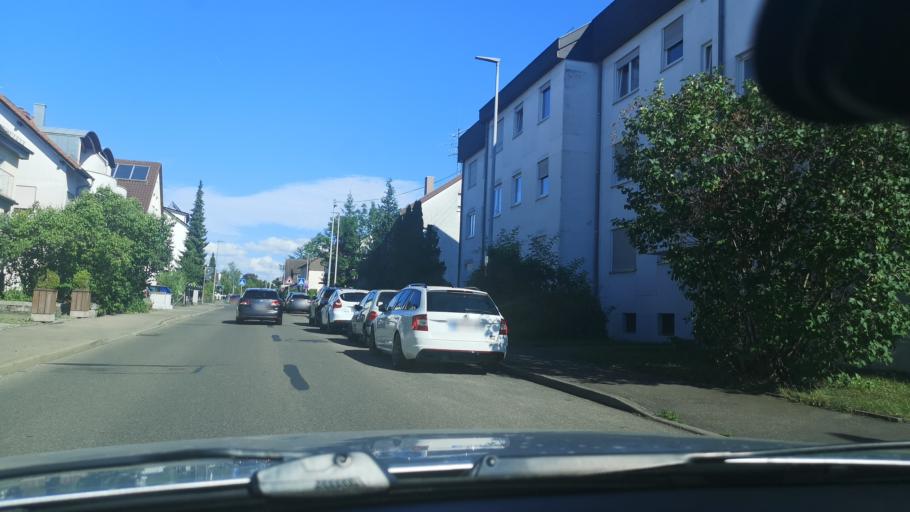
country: DE
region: Baden-Wuerttemberg
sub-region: Regierungsbezirk Stuttgart
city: Eislingen
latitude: 48.6910
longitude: 9.7009
